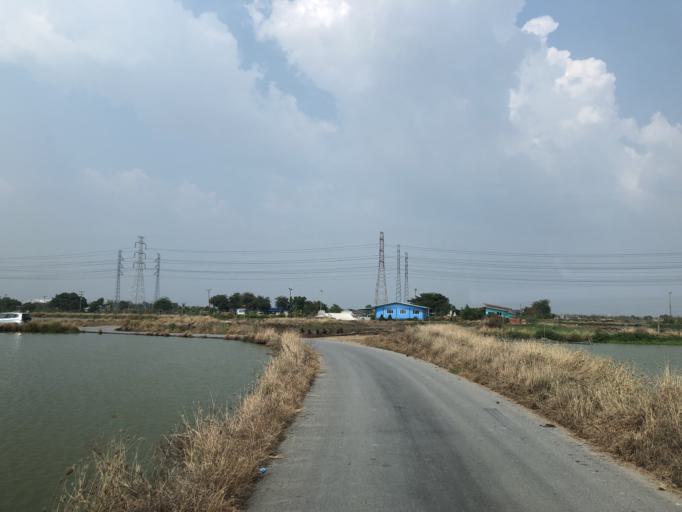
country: TH
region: Samut Prakan
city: Bang Bo
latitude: 13.5428
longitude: 100.8807
